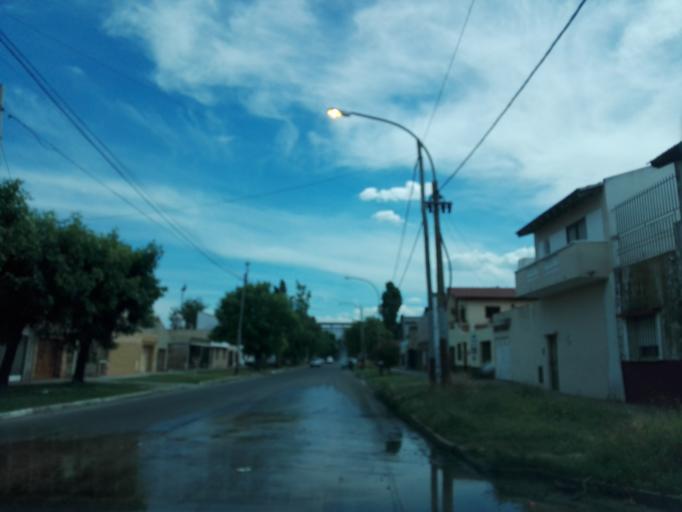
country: AR
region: Buenos Aires
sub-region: Partido de Lanus
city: Lanus
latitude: -34.7154
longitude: -58.3816
